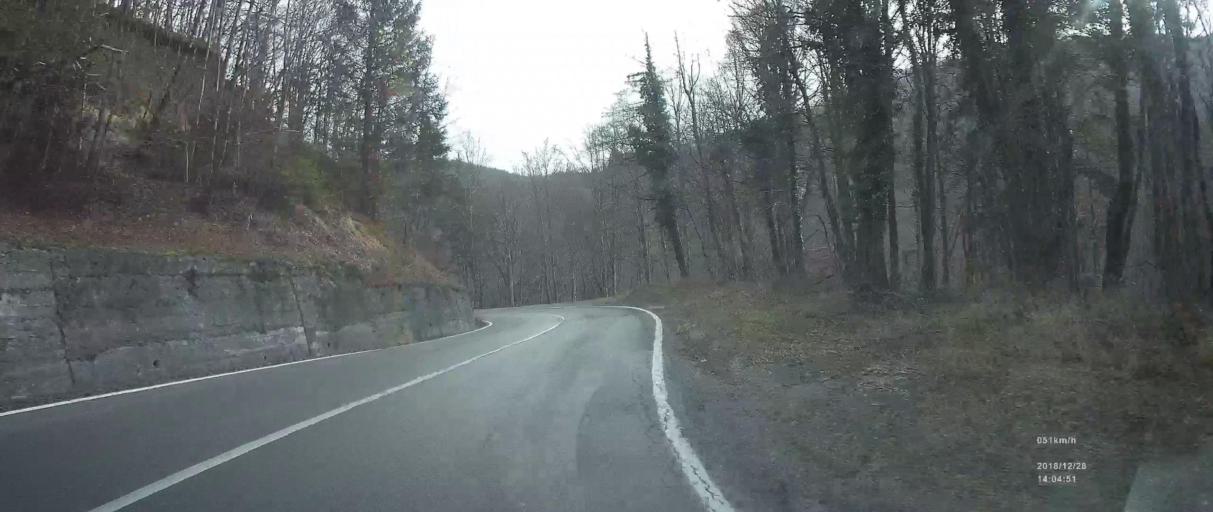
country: SI
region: Kostel
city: Kostel
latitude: 45.4396
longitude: 14.9220
